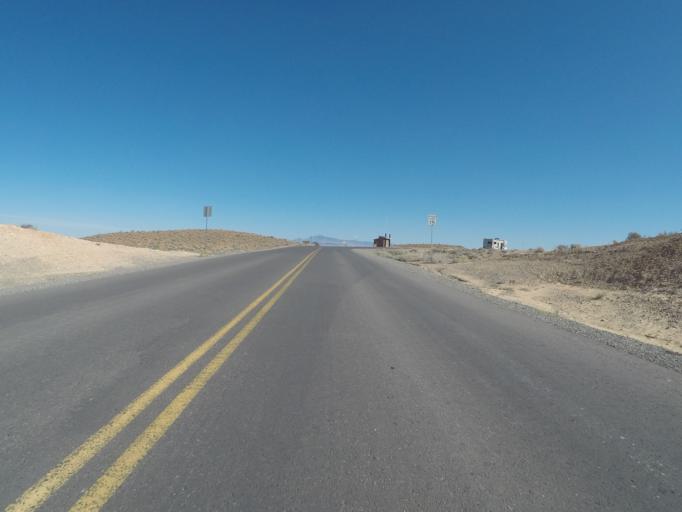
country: US
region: Nevada
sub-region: Clark County
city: Moapa Valley
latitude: 36.4554
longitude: -114.5036
